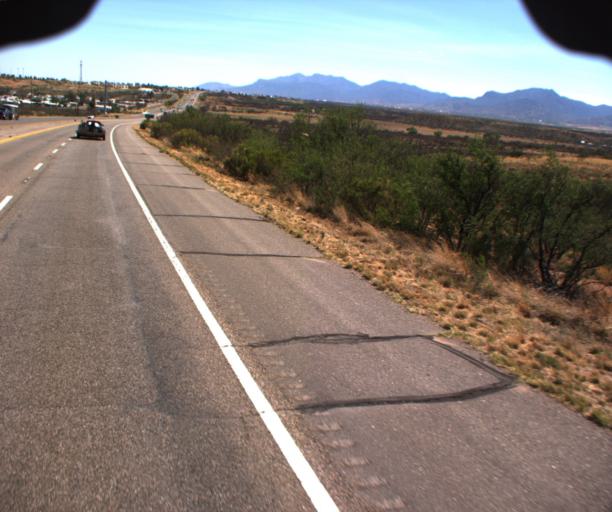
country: US
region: Arizona
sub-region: Cochise County
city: Huachuca City
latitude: 31.6499
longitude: -110.3426
